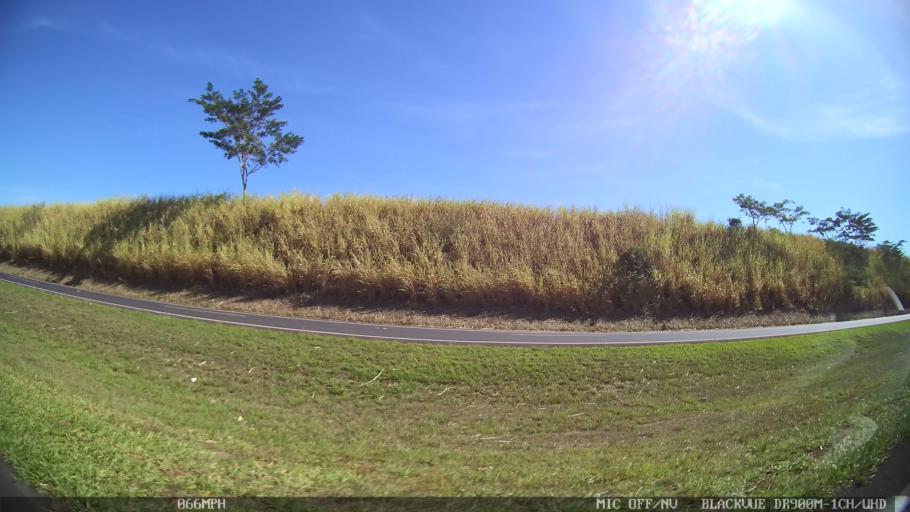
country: BR
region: Sao Paulo
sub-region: Sao Simao
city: Sao Simao
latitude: -21.4769
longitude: -47.6404
